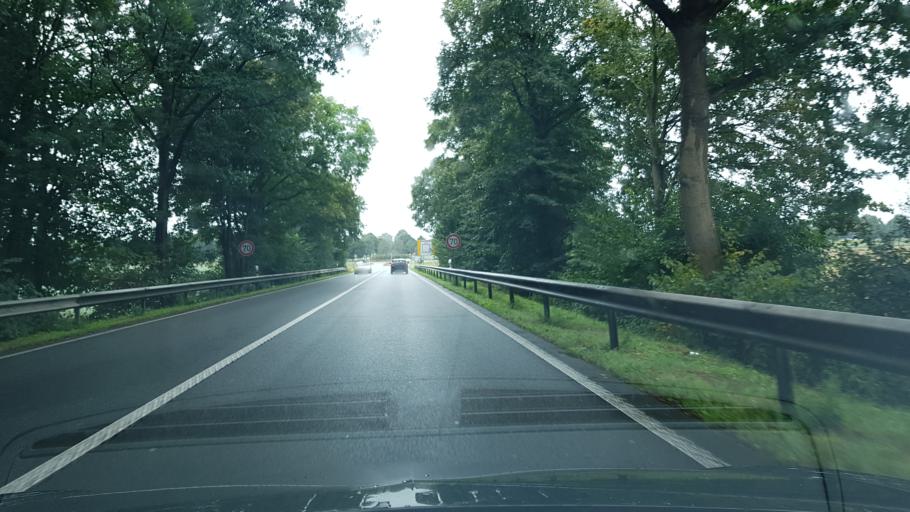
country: DE
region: North Rhine-Westphalia
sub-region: Regierungsbezirk Dusseldorf
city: Nettetal
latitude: 51.3084
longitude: 6.2151
